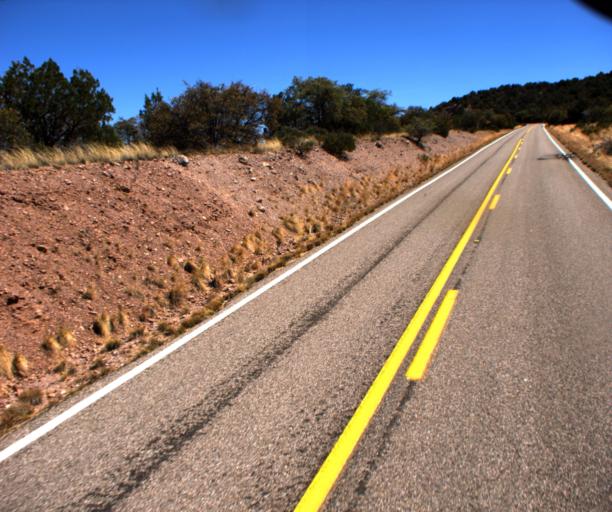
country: US
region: Arizona
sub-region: Cochise County
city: Sierra Vista
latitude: 31.4866
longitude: -110.4851
